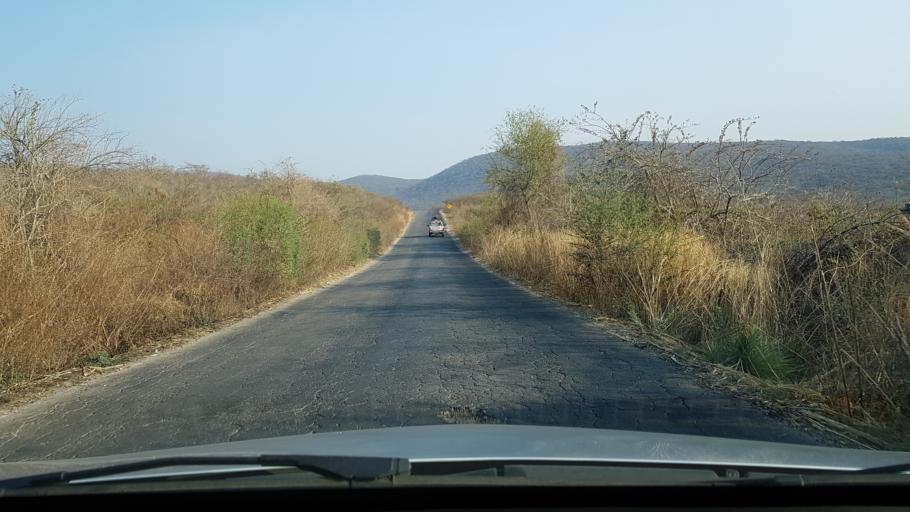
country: MX
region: Morelos
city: Tlaltizapan
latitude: 18.6680
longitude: -99.0532
